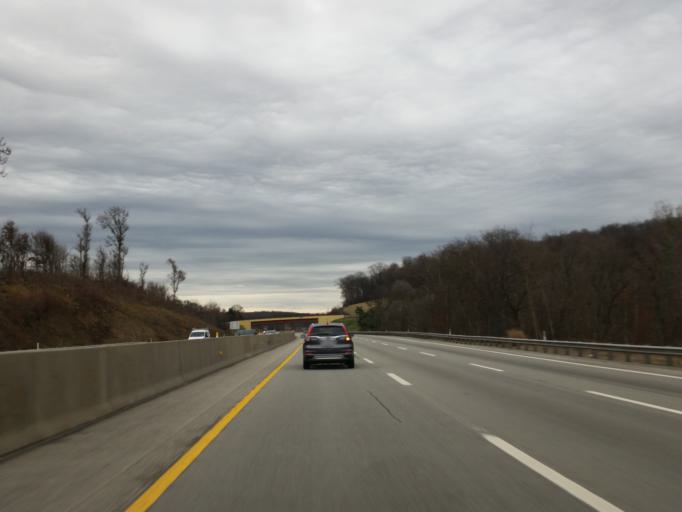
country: US
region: Pennsylvania
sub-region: Fayette County
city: Bear Rocks
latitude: 40.1423
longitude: -79.4180
